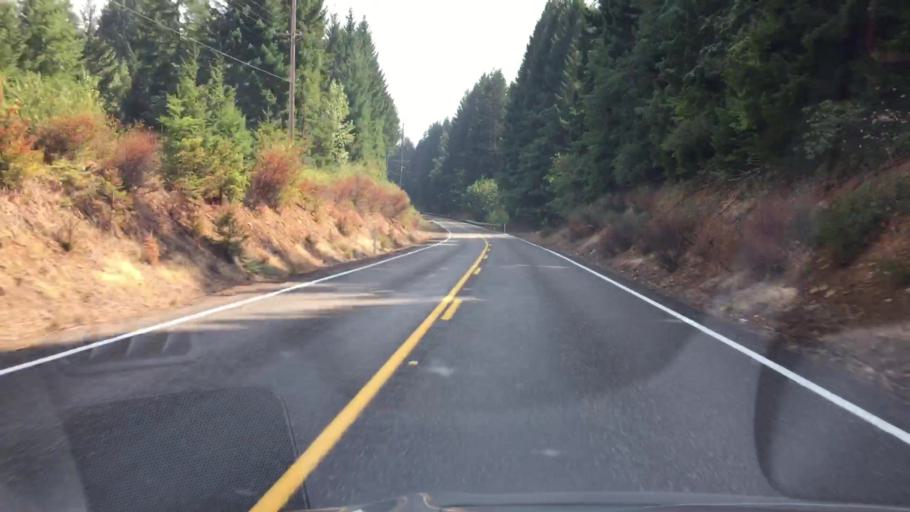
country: US
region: Washington
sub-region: Klickitat County
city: White Salmon
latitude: 45.8785
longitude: -121.5204
